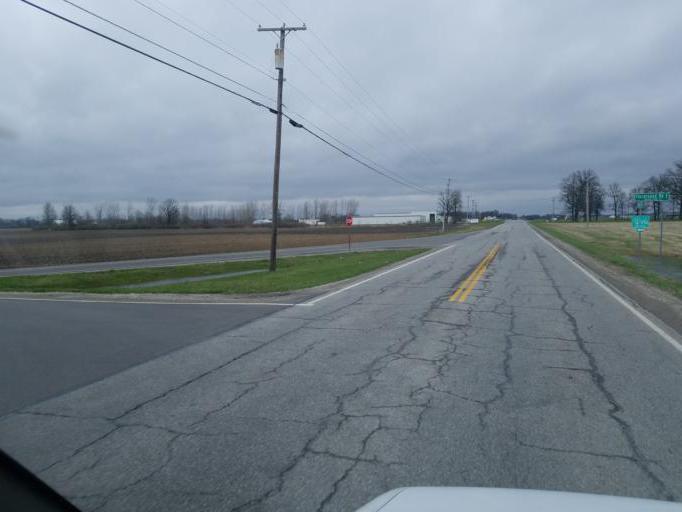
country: US
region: Ohio
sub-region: Marion County
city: Marion
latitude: 40.6052
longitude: -83.0735
